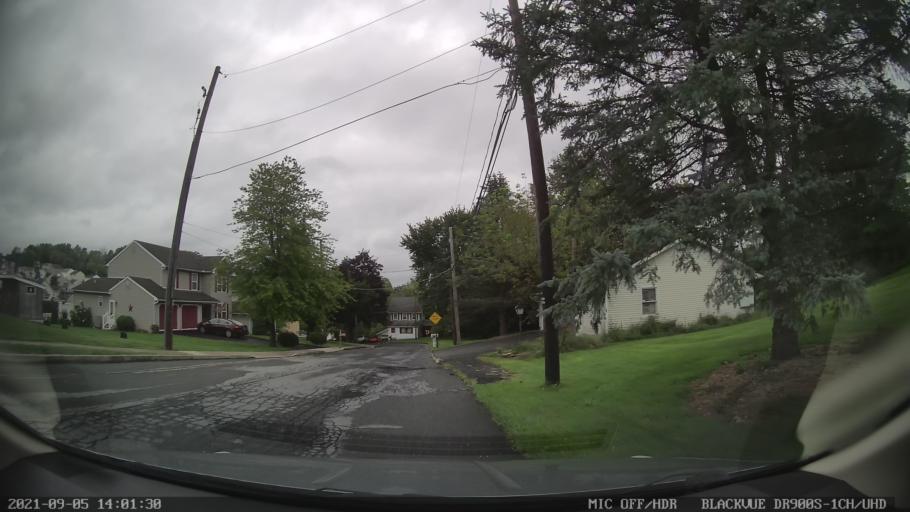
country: US
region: Pennsylvania
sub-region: Northampton County
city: Northampton
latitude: 40.6792
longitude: -75.5023
